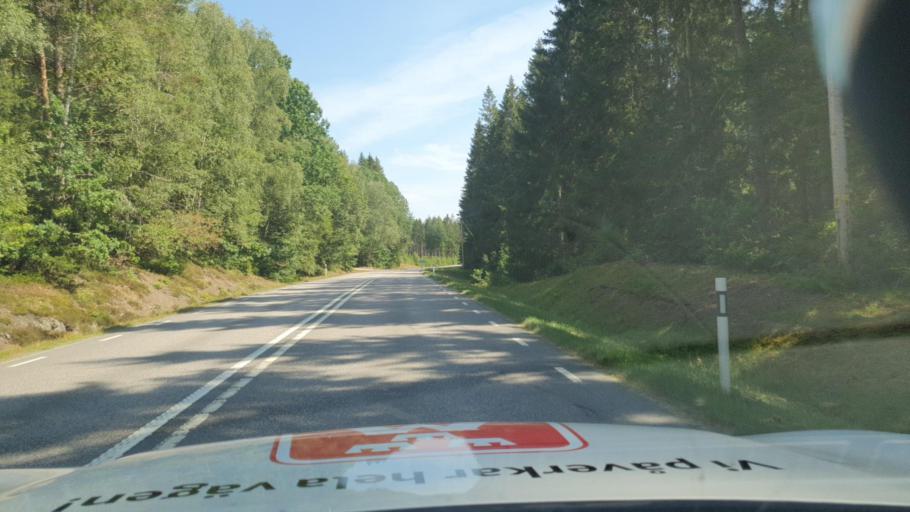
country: SE
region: Vaestra Goetaland
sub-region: Vargarda Kommun
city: Jonstorp
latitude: 58.0848
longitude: 12.6660
